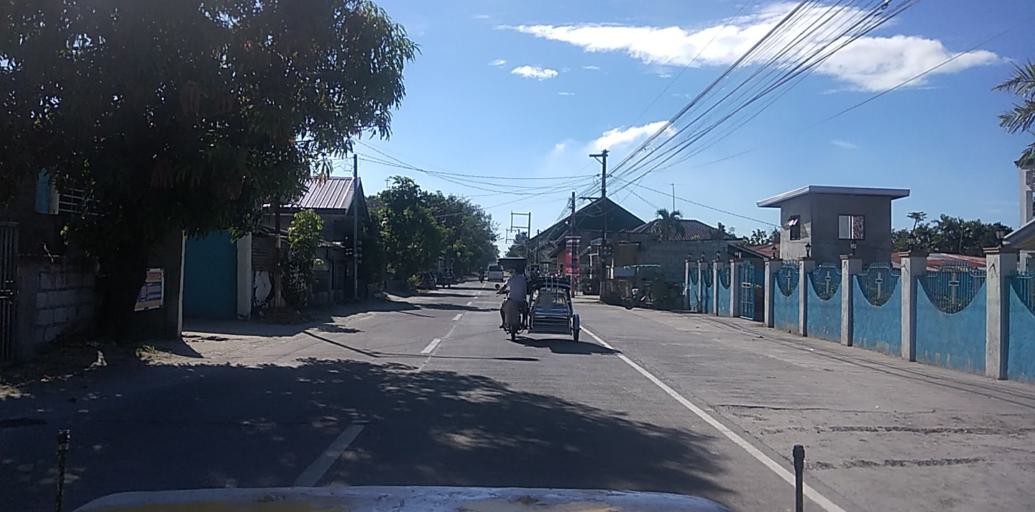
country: PH
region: Central Luzon
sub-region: Province of Pampanga
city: San Patricio
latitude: 15.0859
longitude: 120.7149
